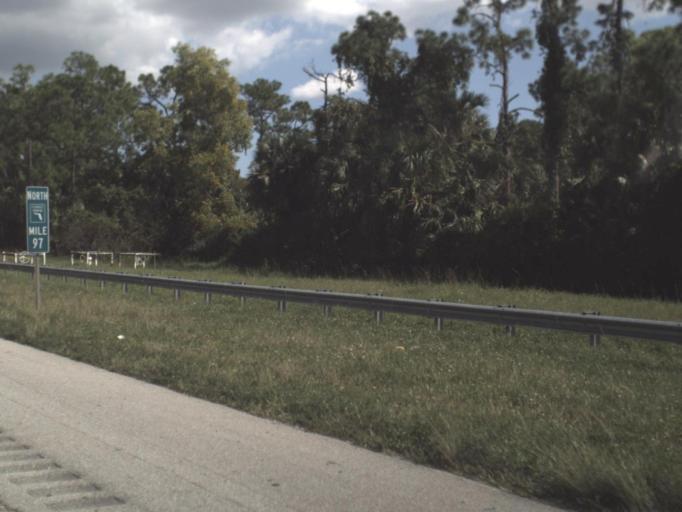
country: US
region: Florida
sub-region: Palm Beach County
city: Lake Belvedere Estates
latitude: 26.6728
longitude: -80.1708
